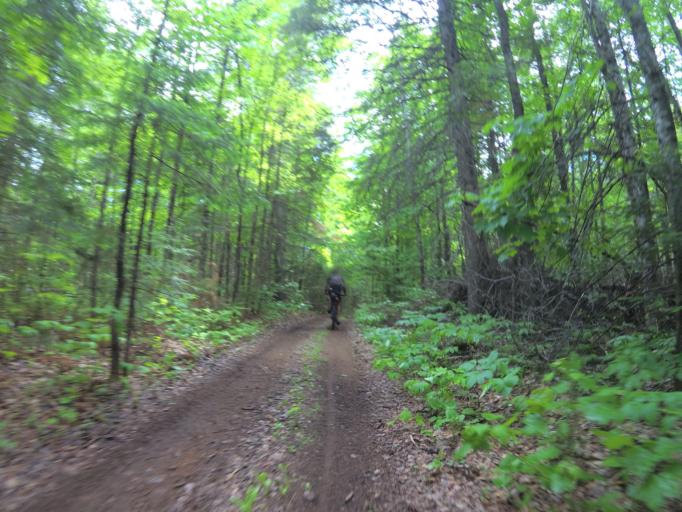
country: CA
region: Ontario
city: Renfrew
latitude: 45.1156
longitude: -76.8525
